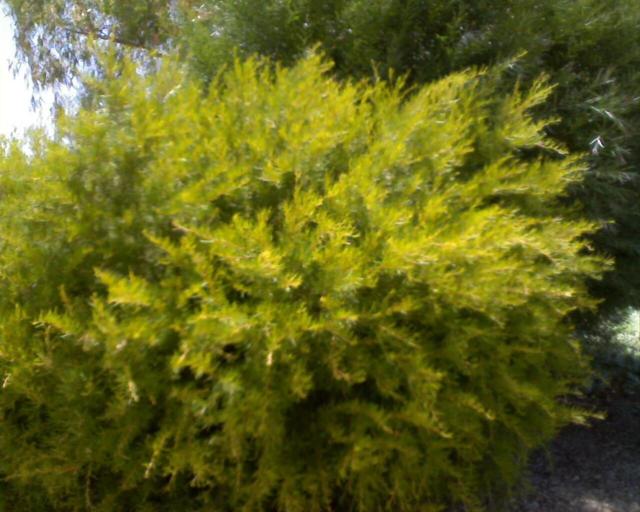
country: AU
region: Western Australia
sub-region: Wongan-Ballidu
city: Wongan Hills
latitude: -30.8208
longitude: 117.4844
